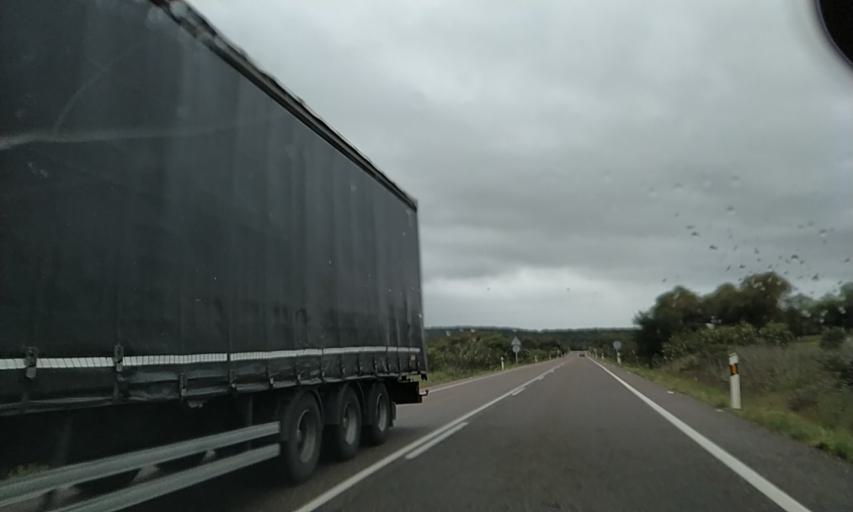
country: ES
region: Extremadura
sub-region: Provincia de Badajoz
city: Puebla de Obando
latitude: 39.1463
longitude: -6.6525
